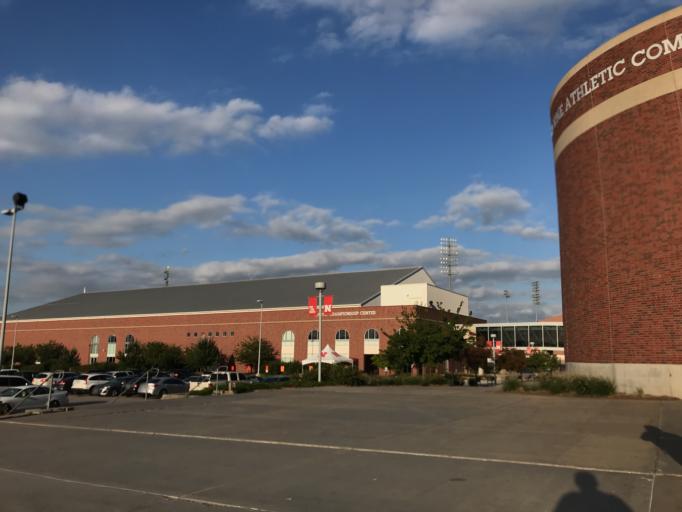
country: US
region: Nebraska
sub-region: Lancaster County
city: Lincoln
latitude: 40.8219
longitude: -96.7064
